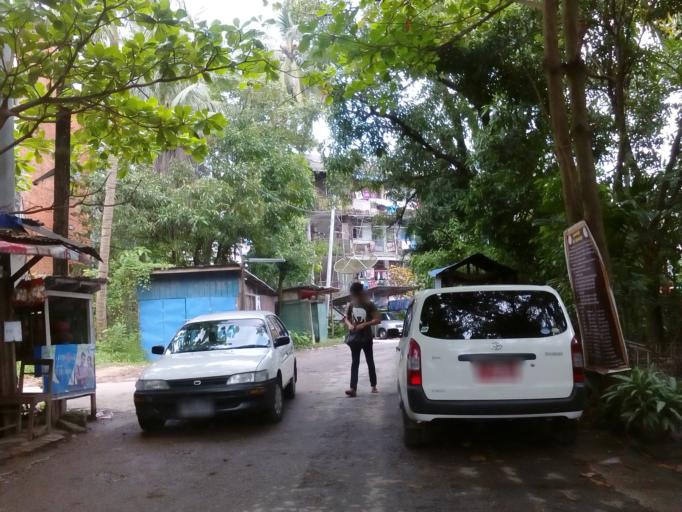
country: MM
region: Yangon
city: Yangon
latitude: 16.8263
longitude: 96.1587
